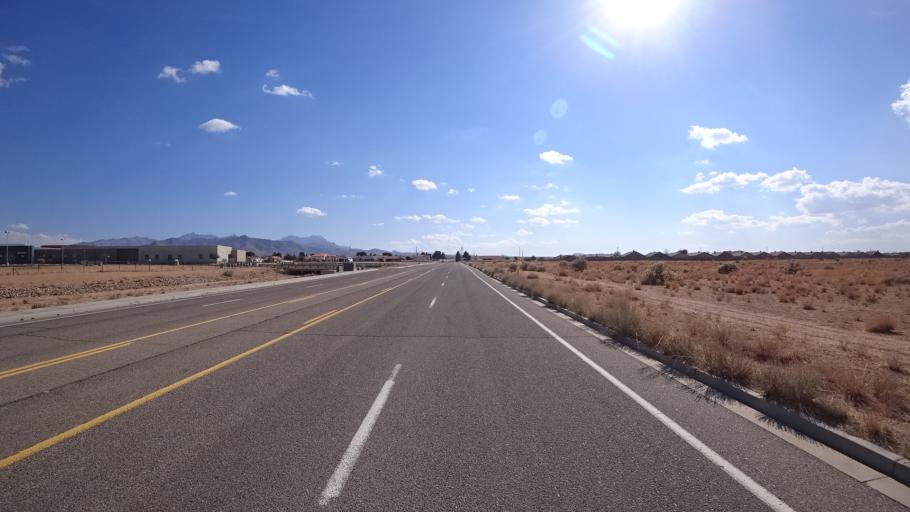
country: US
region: Arizona
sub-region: Mohave County
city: New Kingman-Butler
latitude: 35.2276
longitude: -113.9762
